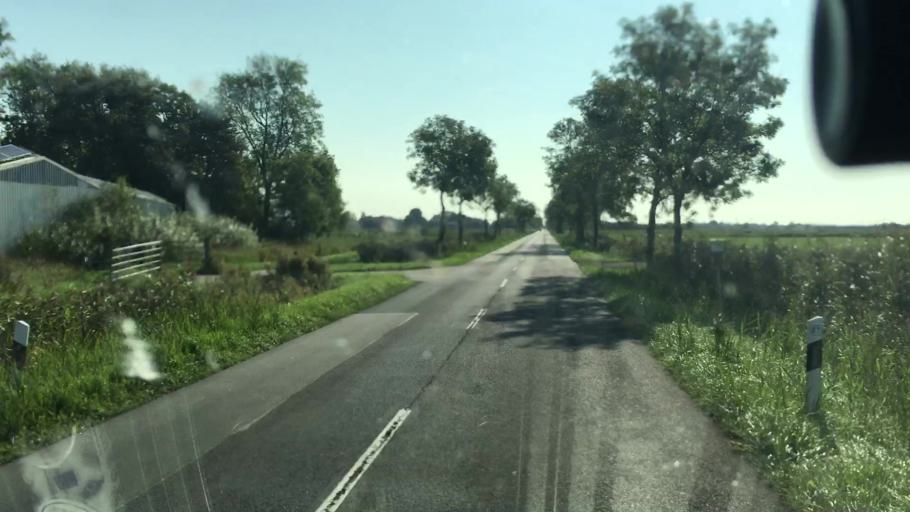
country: DE
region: Lower Saxony
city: Werdum
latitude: 53.6659
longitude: 7.6834
